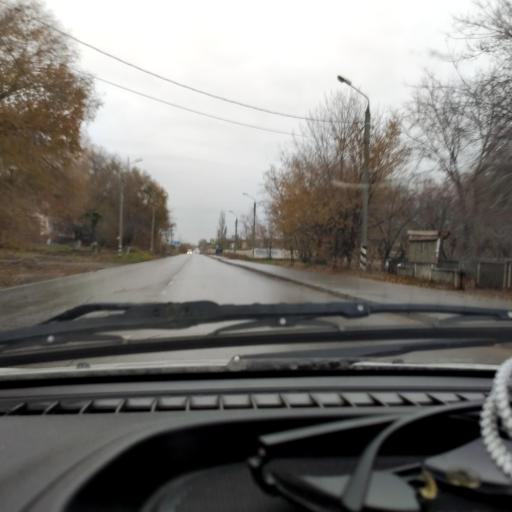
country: RU
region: Samara
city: Zhigulevsk
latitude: 53.4646
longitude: 49.5389
